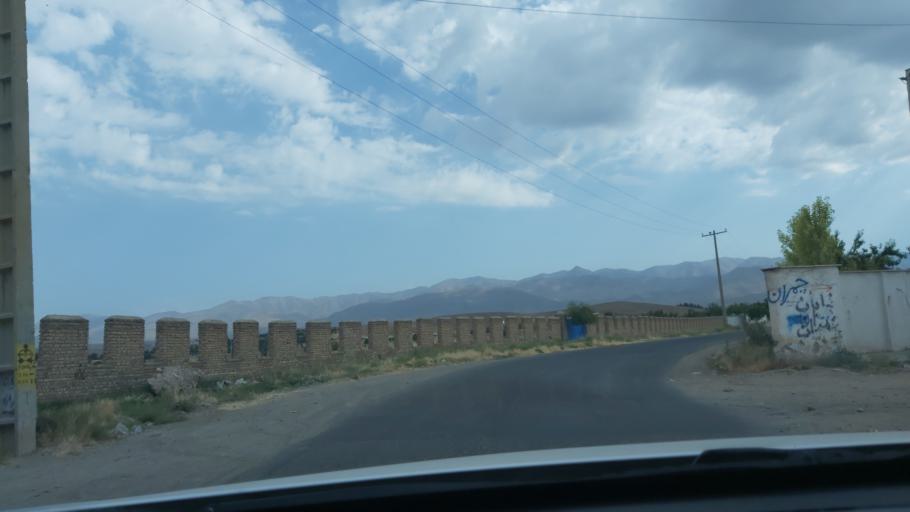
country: IR
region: Alborz
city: Hashtgerd
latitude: 35.9525
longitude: 50.7757
